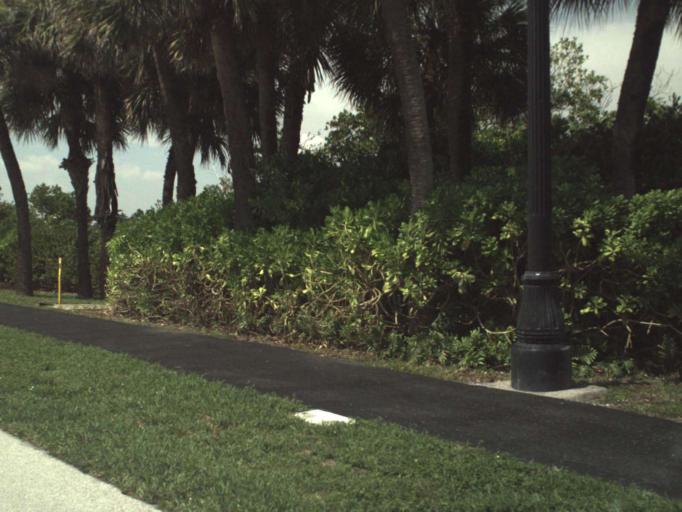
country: US
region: Florida
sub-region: Palm Beach County
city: South Palm Beach
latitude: 26.5977
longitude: -80.0387
